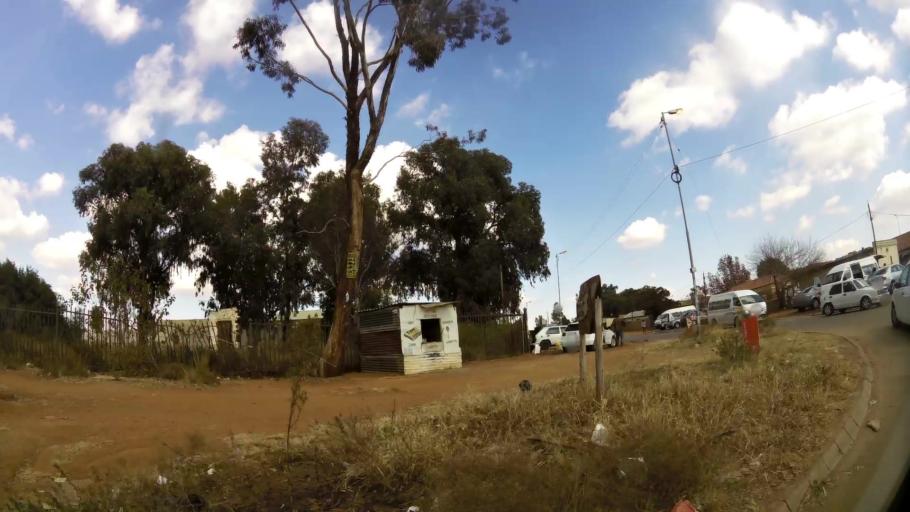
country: ZA
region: Gauteng
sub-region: City of Tshwane Metropolitan Municipality
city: Cullinan
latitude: -25.7029
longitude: 28.4144
